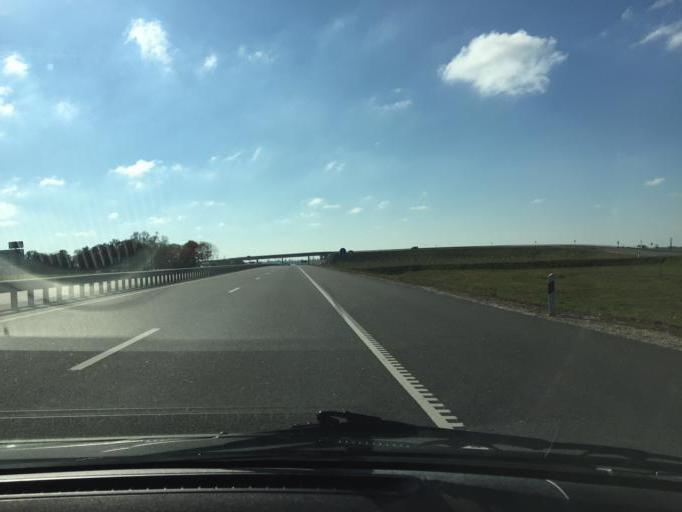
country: BY
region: Minsk
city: Slutsk
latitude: 53.0708
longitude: 27.5556
